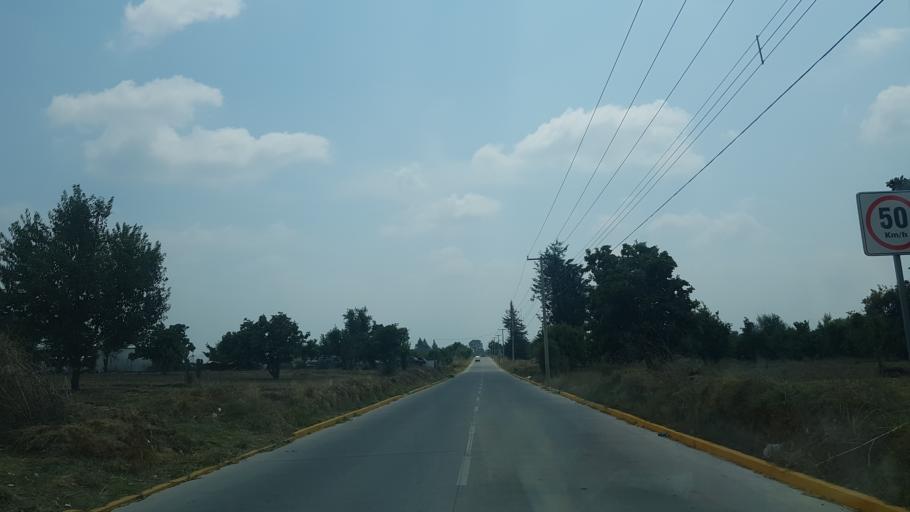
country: MX
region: Puebla
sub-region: Huejotzingo
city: San Juan Pancoac
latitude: 19.1385
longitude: -98.4350
